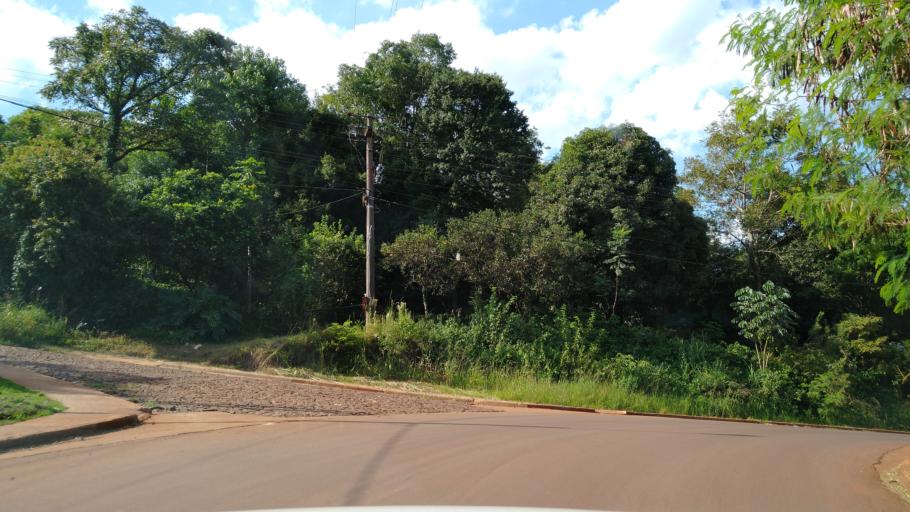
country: AR
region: Misiones
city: Puerto Piray
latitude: -26.4664
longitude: -54.7050
